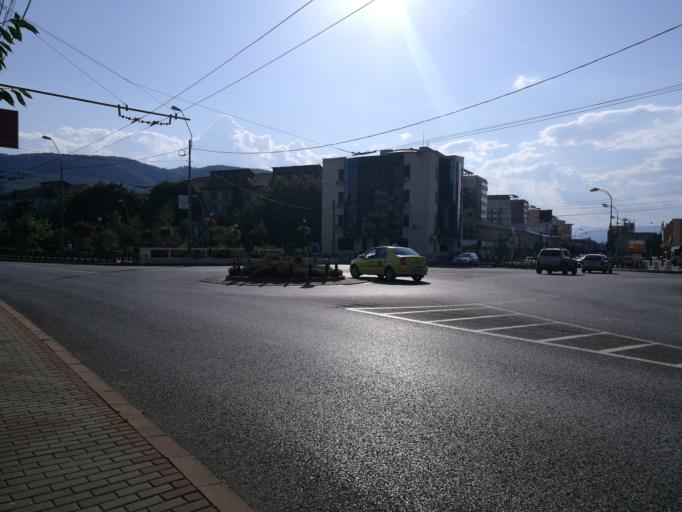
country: RO
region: Neamt
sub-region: Municipiul Piatra-Neamt
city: Valeni
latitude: 46.9314
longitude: 26.3737
